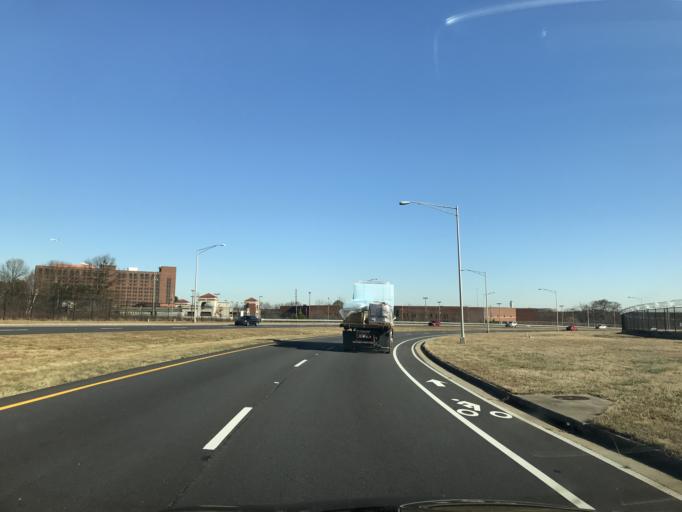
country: US
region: Georgia
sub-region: Fulton County
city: College Park
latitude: 33.6208
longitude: -84.4519
